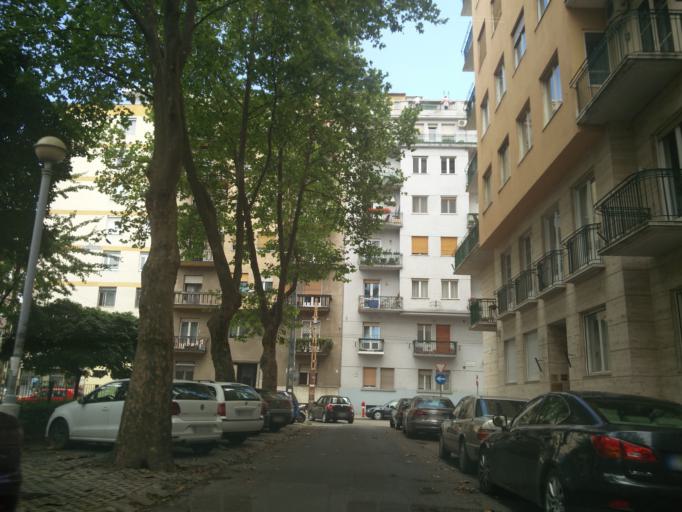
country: HU
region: Budapest
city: Budapest VI. keruelet
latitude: 47.5178
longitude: 19.0520
